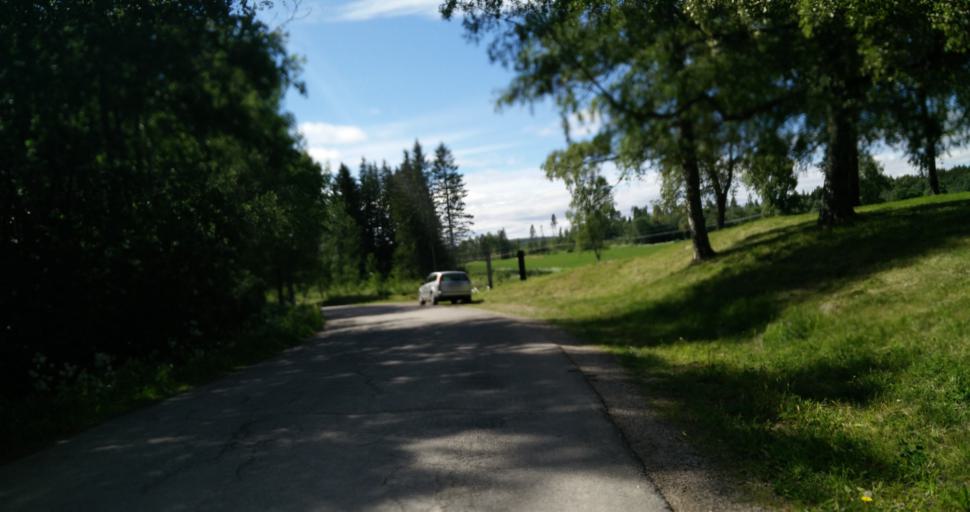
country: SE
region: Vaesternorrland
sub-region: Sundsvalls Kommun
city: Nolby
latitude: 62.2845
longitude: 17.3653
